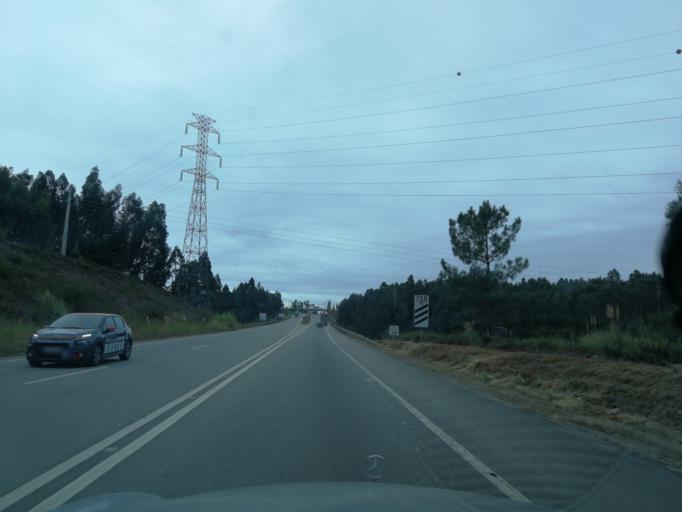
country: PT
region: Aveiro
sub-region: Agueda
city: Valongo
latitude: 40.6023
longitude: -8.4675
